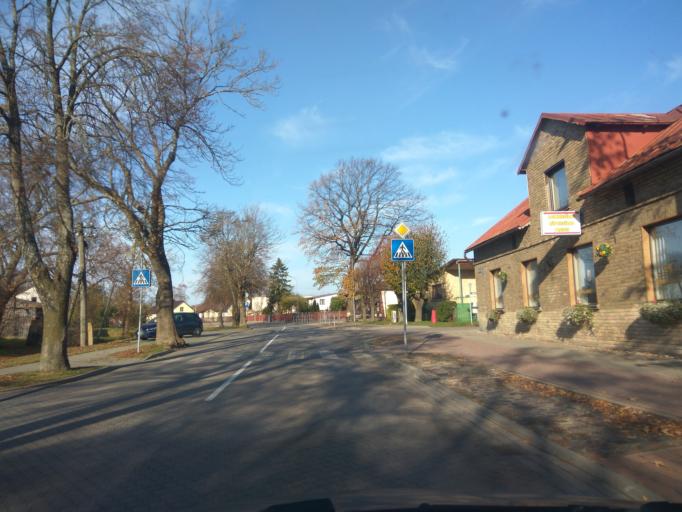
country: LV
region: Ventspils
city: Ventspils
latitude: 57.3776
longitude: 21.5733
